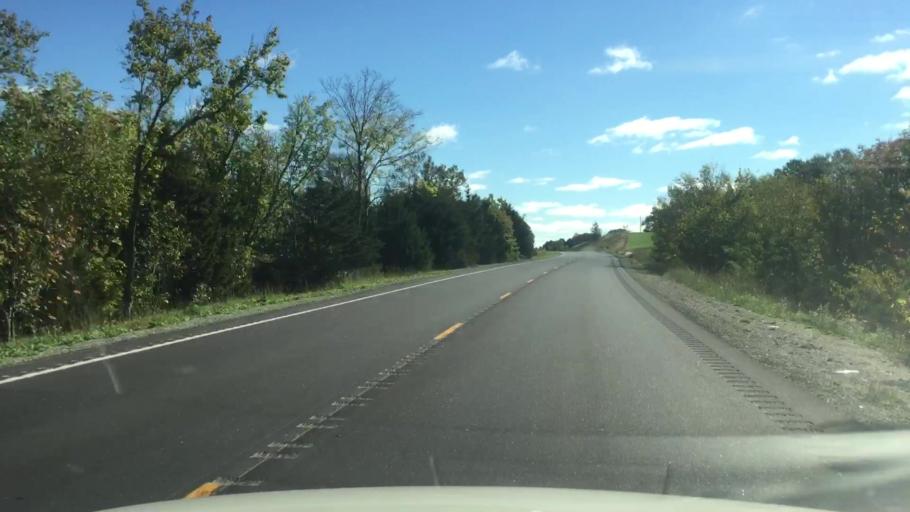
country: US
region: Missouri
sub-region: Boone County
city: Columbia
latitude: 38.9896
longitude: -92.5079
